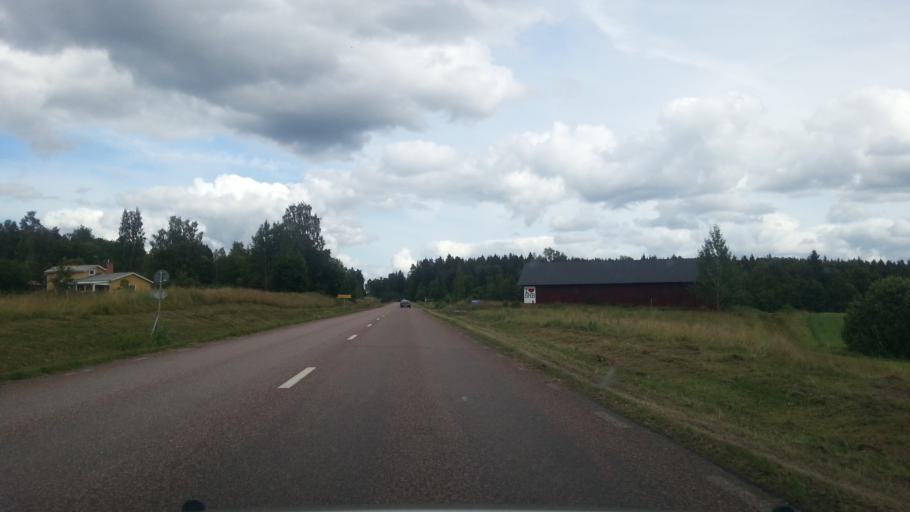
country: SE
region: Dalarna
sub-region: Smedjebackens Kommun
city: Smedjebacken
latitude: 60.1597
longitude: 15.4366
